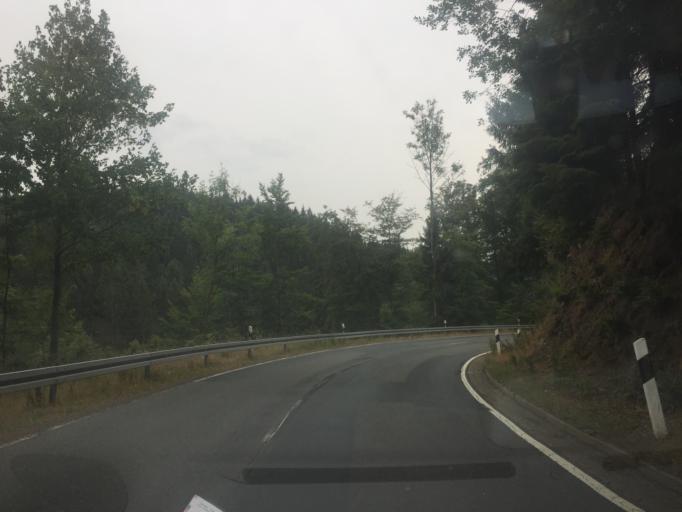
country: DE
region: Lower Saxony
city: Wieda
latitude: 51.6669
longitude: 10.5922
